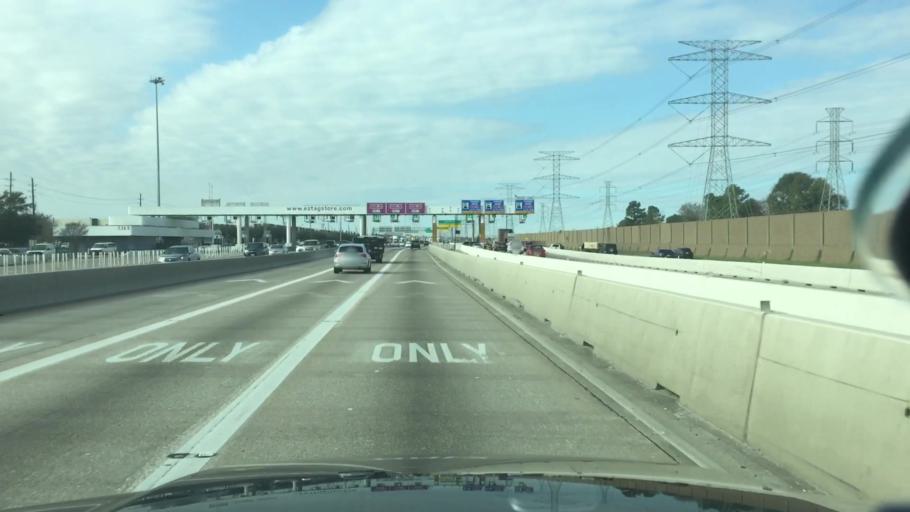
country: US
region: Texas
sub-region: Harris County
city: Hudson
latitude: 29.9377
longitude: -95.4700
